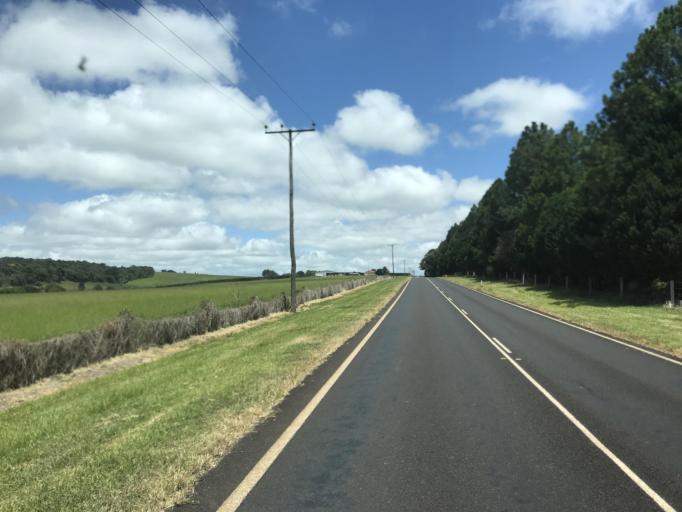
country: AU
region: Queensland
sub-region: Tablelands
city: Ravenshoe
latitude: -17.5077
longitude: 145.4601
